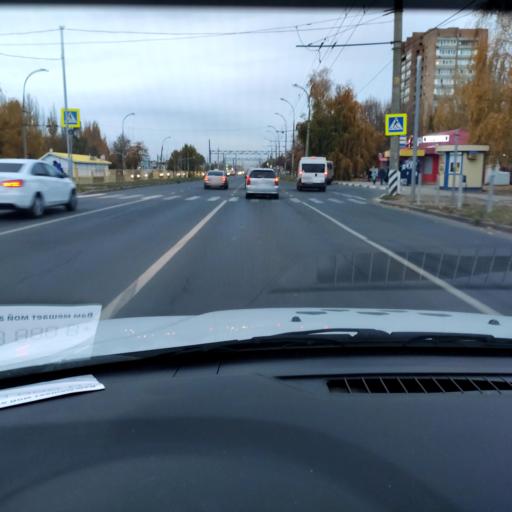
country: RU
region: Samara
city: Tol'yatti
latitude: 53.5342
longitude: 49.2990
